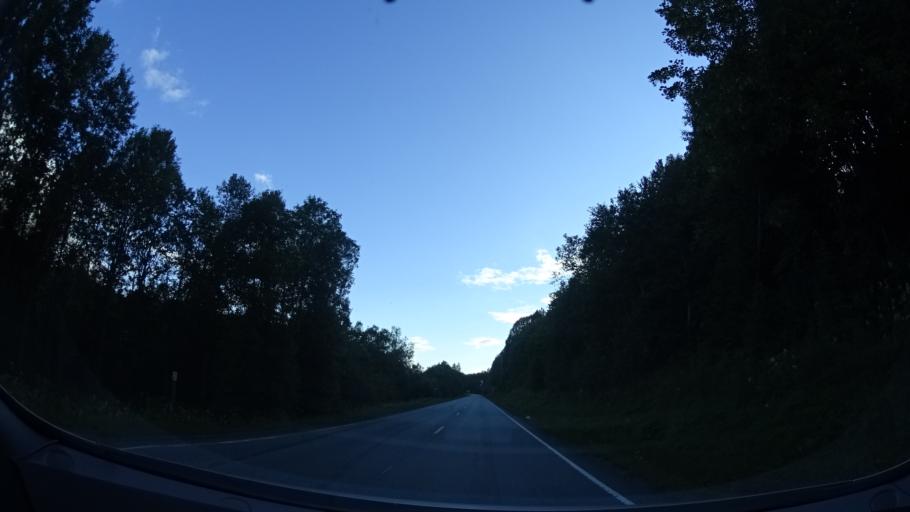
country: NO
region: More og Romsdal
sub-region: Molde
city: Hjelset
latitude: 62.7910
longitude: 7.5303
